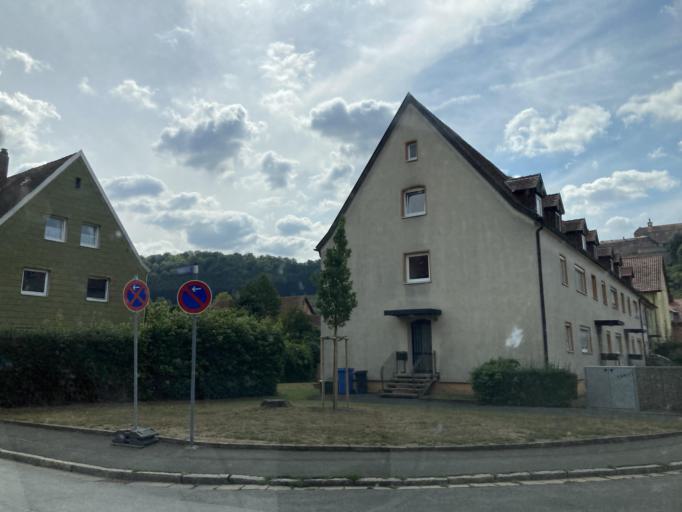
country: DE
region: Bavaria
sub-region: Upper Franconia
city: Kulmbach
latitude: 50.1141
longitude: 11.4656
